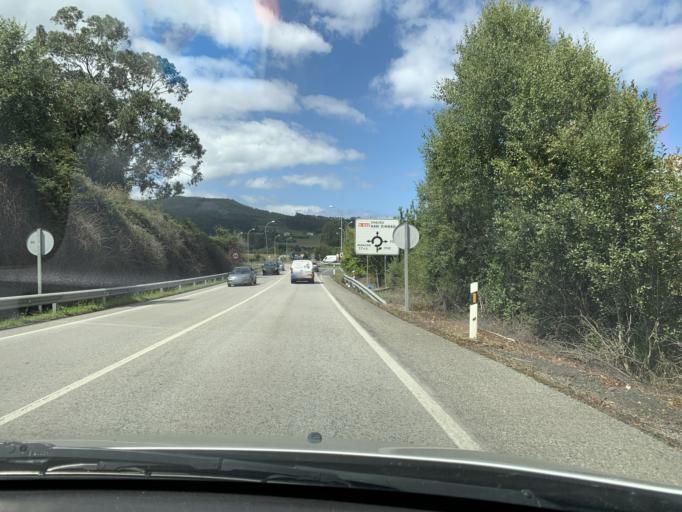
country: ES
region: Galicia
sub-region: Provincia de Lugo
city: Foz
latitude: 43.5612
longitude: -7.2716
